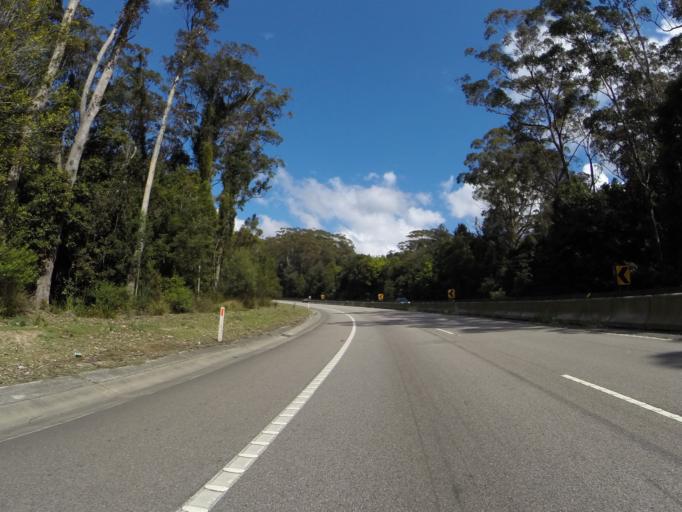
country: AU
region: New South Wales
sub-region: Wollongong
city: Mount Ousley
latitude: -34.3637
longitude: 150.8523
